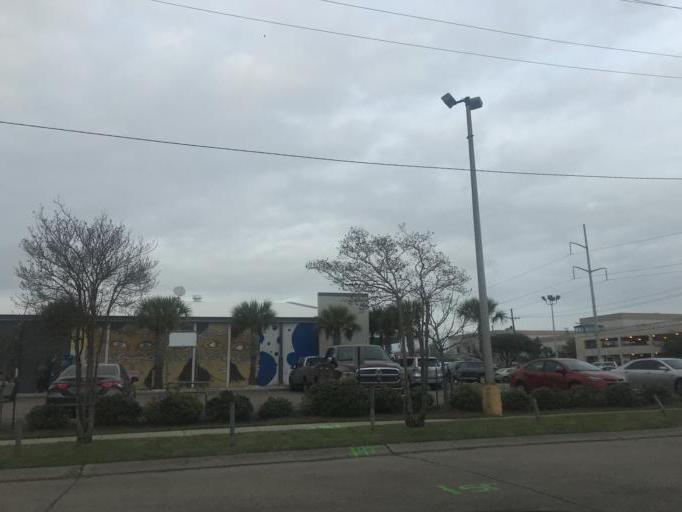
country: US
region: Louisiana
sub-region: Jefferson Parish
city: Metairie
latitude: 30.0045
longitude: -90.1602
